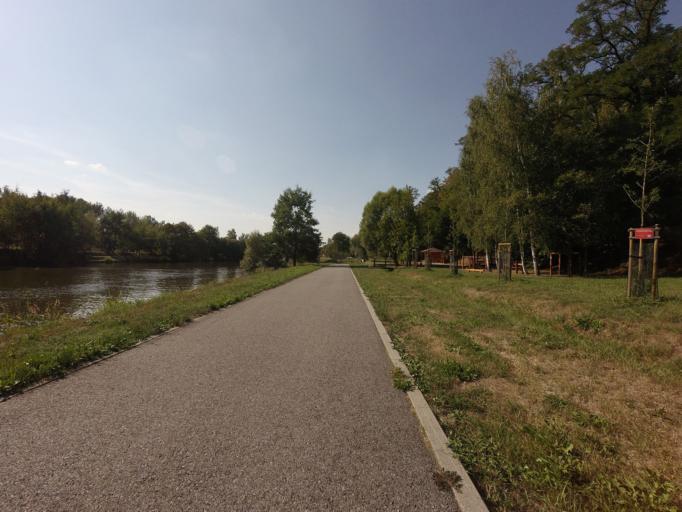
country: CZ
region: Jihocesky
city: Tyn nad Vltavou
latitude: 49.2139
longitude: 14.4387
